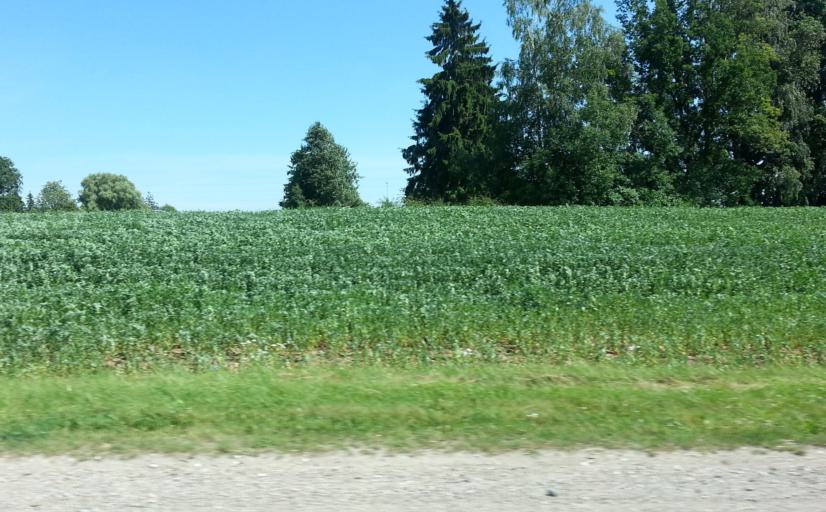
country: LT
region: Panevezys
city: Pasvalys
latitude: 56.0891
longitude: 24.4479
